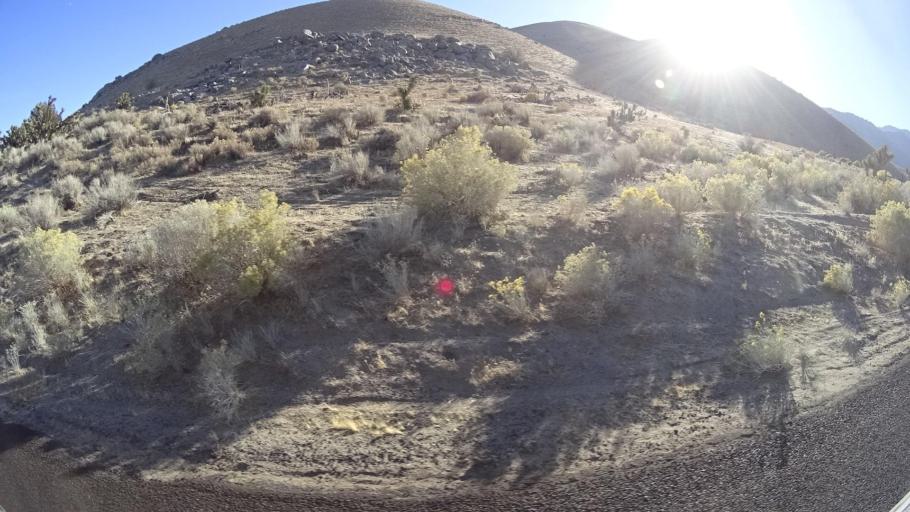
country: US
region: California
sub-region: Kern County
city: Weldon
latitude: 35.6161
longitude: -118.2524
